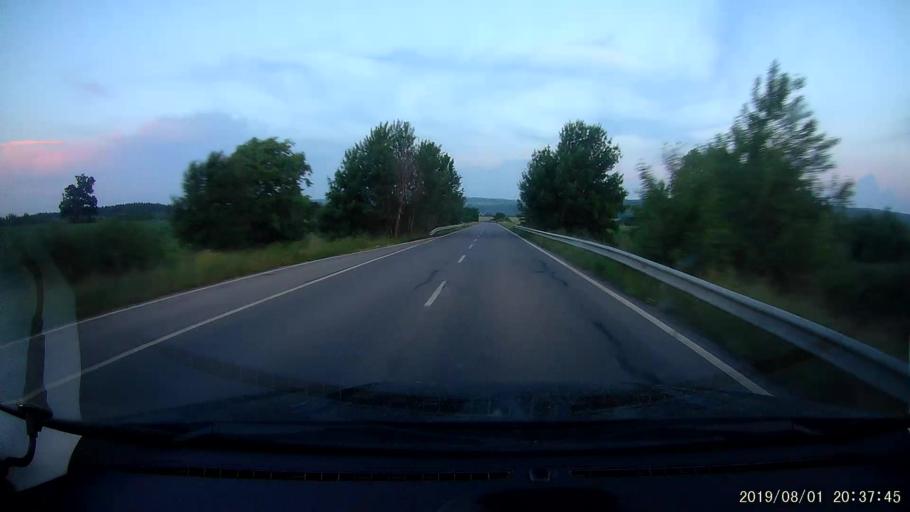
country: BG
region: Yambol
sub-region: Obshtina Elkhovo
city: Elkhovo
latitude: 42.0413
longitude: 26.5955
